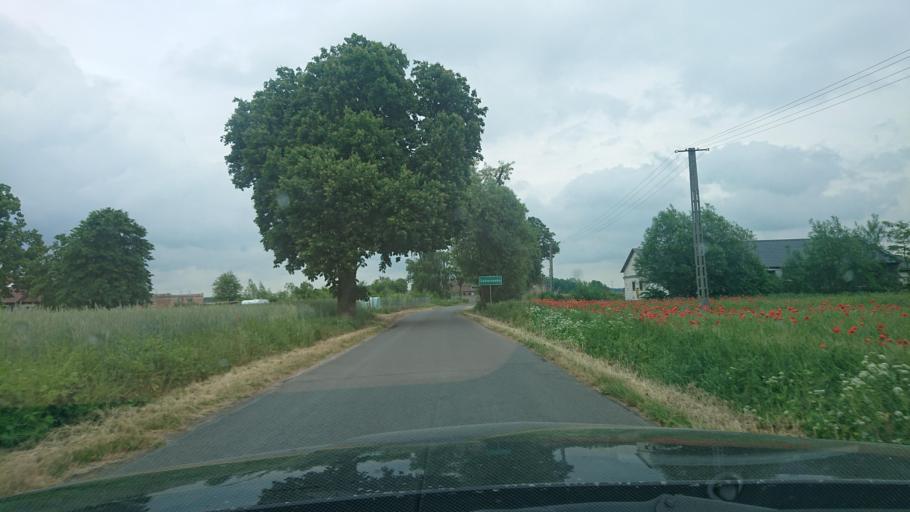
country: PL
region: Greater Poland Voivodeship
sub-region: Powiat gnieznienski
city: Gniezno
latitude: 52.4807
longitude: 17.5414
